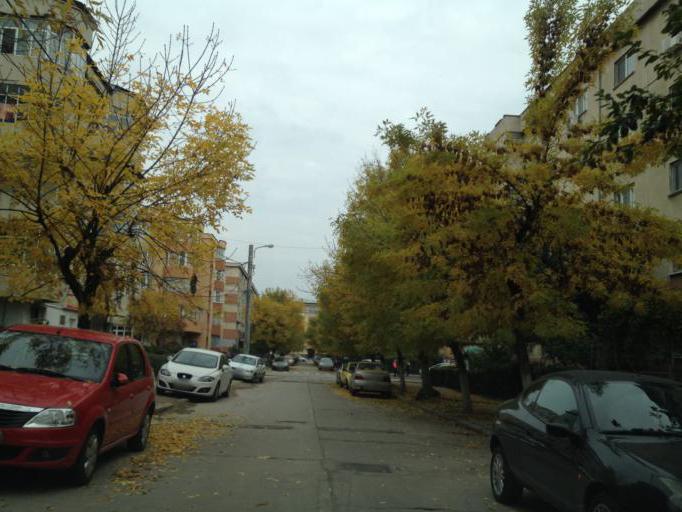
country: RO
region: Dolj
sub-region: Municipiul Craiova
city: Popoveni
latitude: 44.2979
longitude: 23.7928
